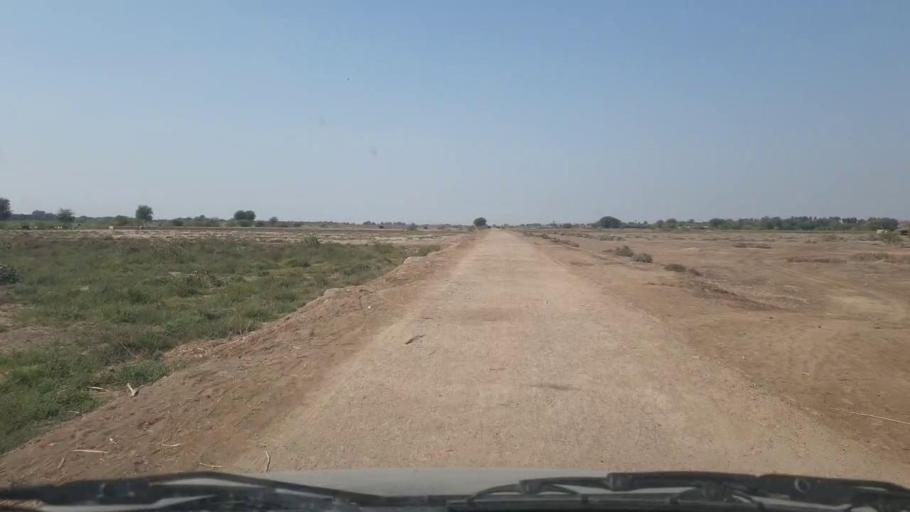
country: PK
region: Sindh
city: Samaro
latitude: 25.2393
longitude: 69.3353
